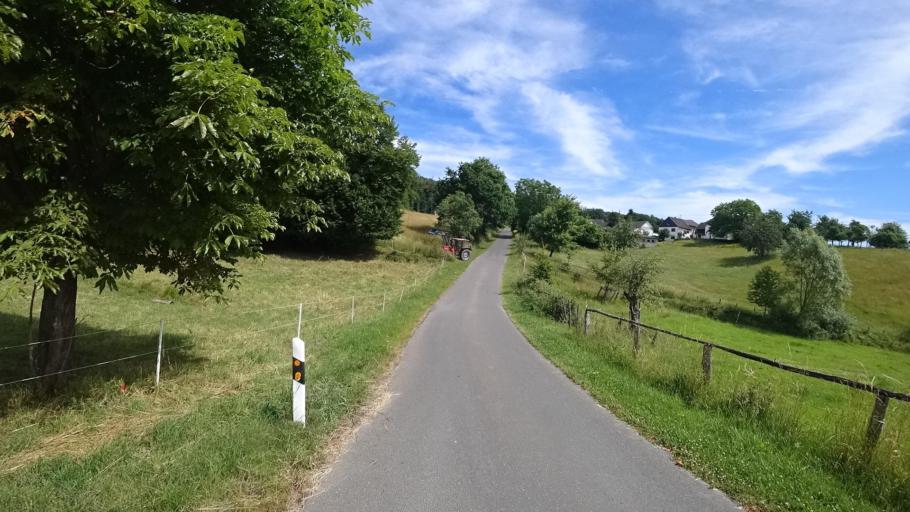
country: DE
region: Rheinland-Pfalz
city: Ratzert
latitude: 50.6544
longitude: 7.6208
